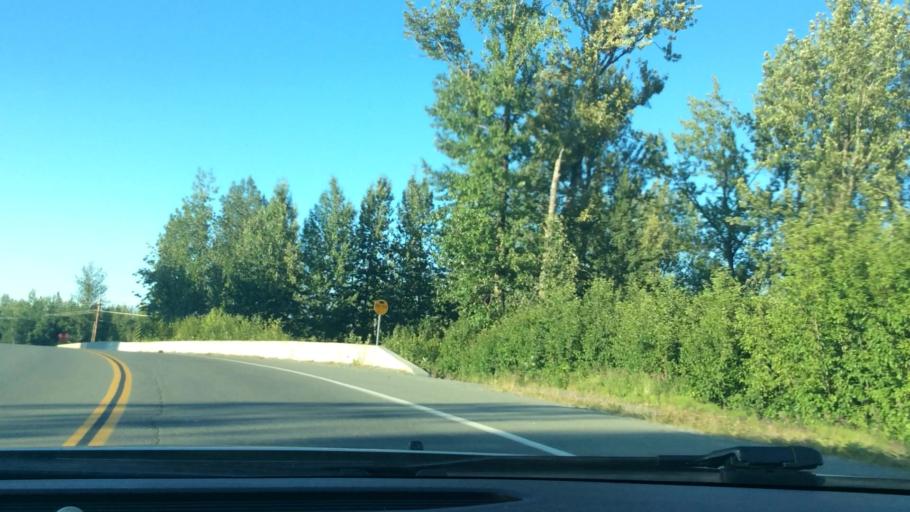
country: US
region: Alaska
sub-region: Anchorage Municipality
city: Elmendorf Air Force Base
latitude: 61.2403
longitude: -149.7085
